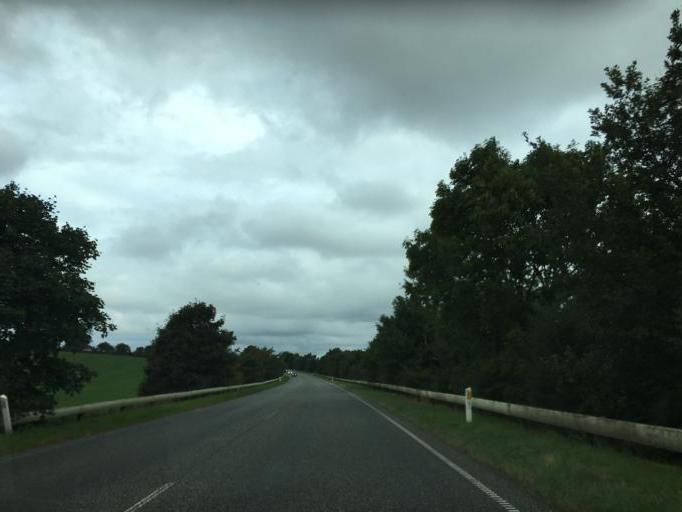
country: DK
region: South Denmark
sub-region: Kolding Kommune
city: Kolding
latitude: 55.5803
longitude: 9.4994
